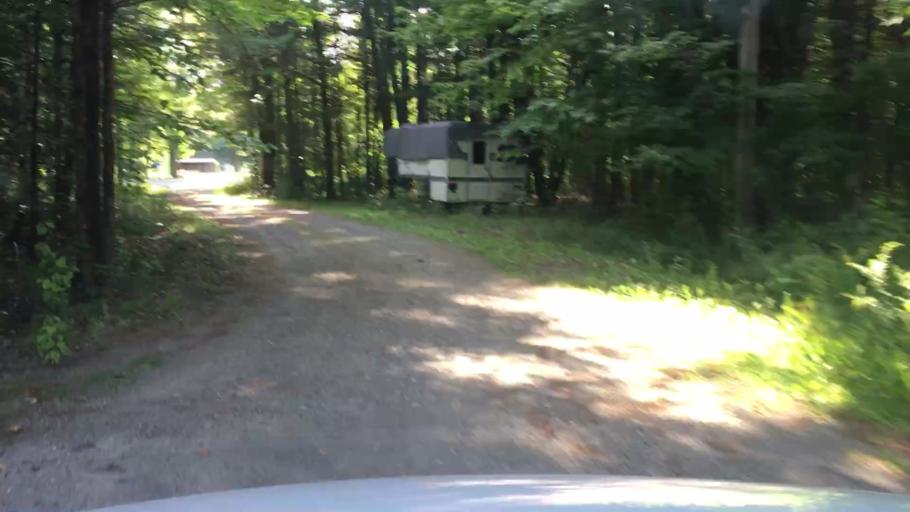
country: US
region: Maine
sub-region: Penobscot County
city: Enfield
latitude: 45.2338
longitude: -68.5426
